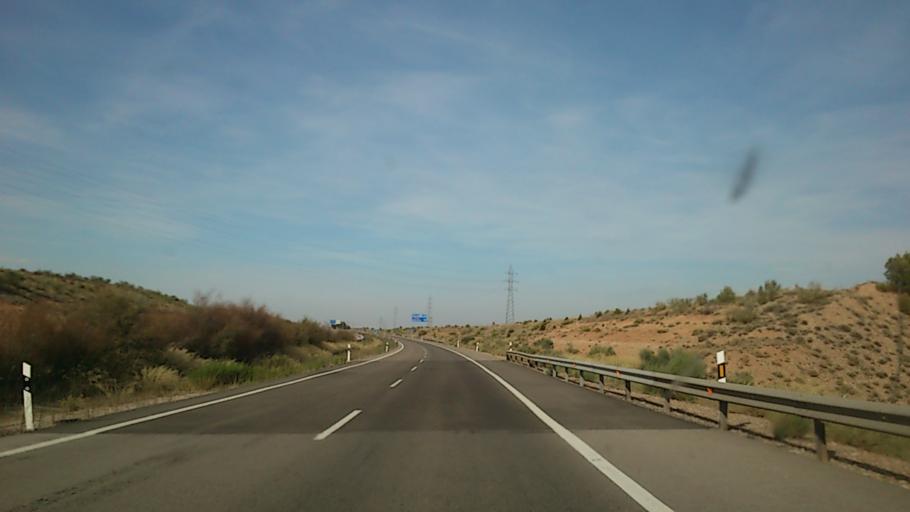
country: ES
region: Aragon
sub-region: Provincia de Zaragoza
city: Botorrita
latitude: 41.5071
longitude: -1.0458
